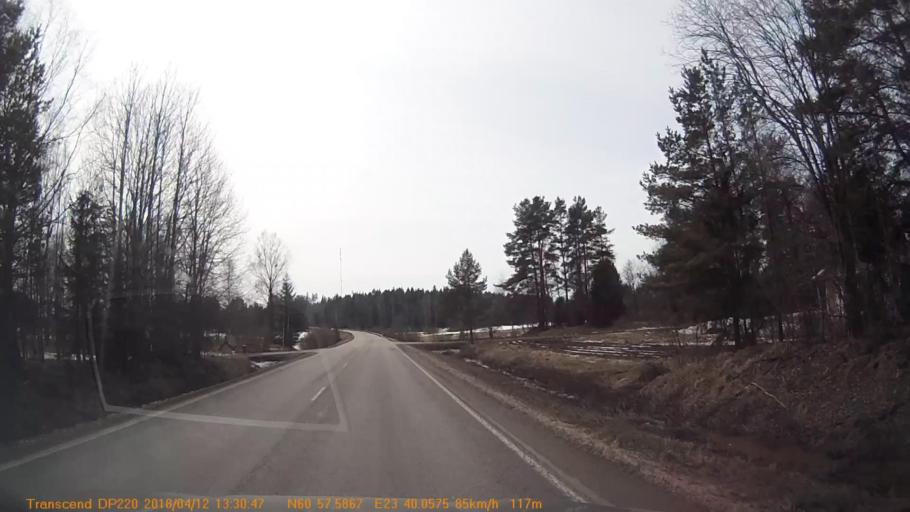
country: FI
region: Haeme
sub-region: Forssa
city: Forssa
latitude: 60.9597
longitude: 23.6675
